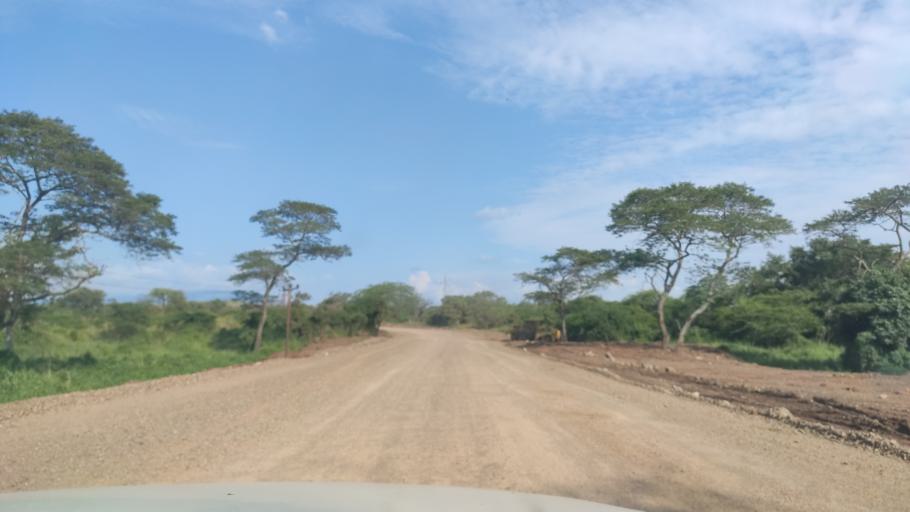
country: ET
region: Southern Nations, Nationalities, and People's Region
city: Felege Neway
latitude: 6.4281
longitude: 37.2067
